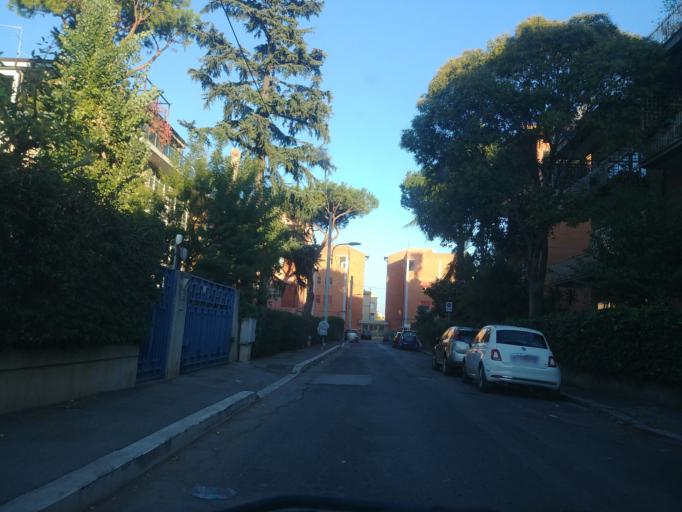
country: IT
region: Latium
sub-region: Provincia di Latina
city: Latina
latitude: 41.4596
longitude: 12.9032
